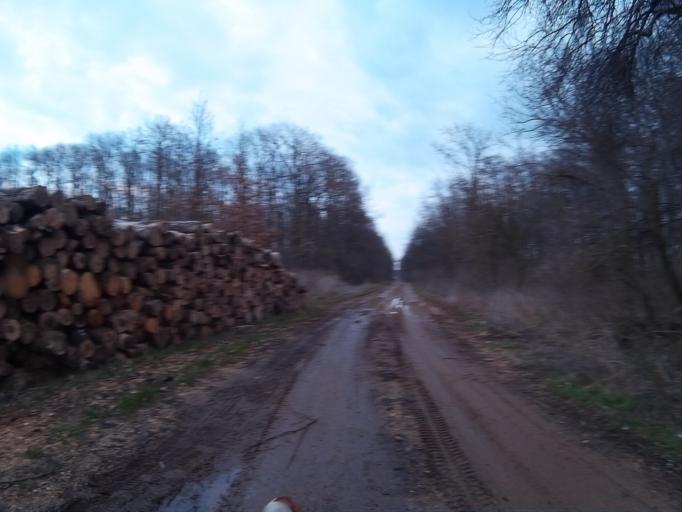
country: HU
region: Vas
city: Janoshaza
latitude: 47.1258
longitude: 17.0355
